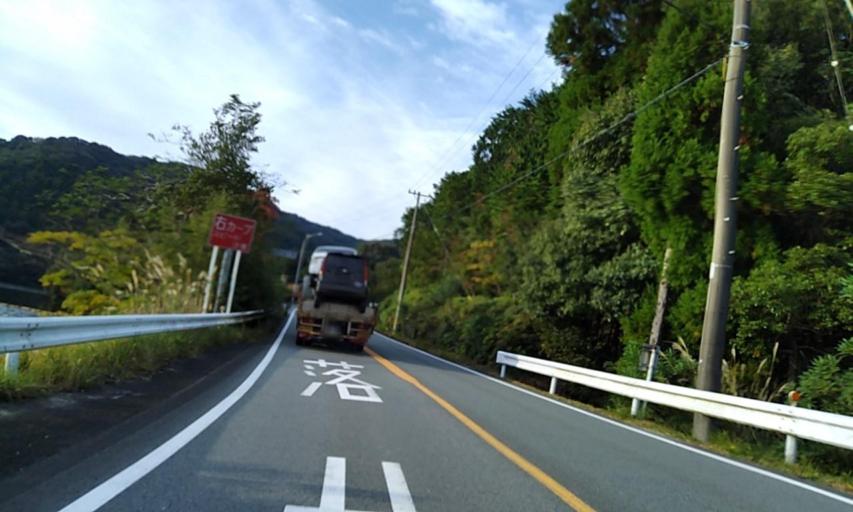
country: JP
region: Mie
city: Toba
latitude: 34.4054
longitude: 136.7756
